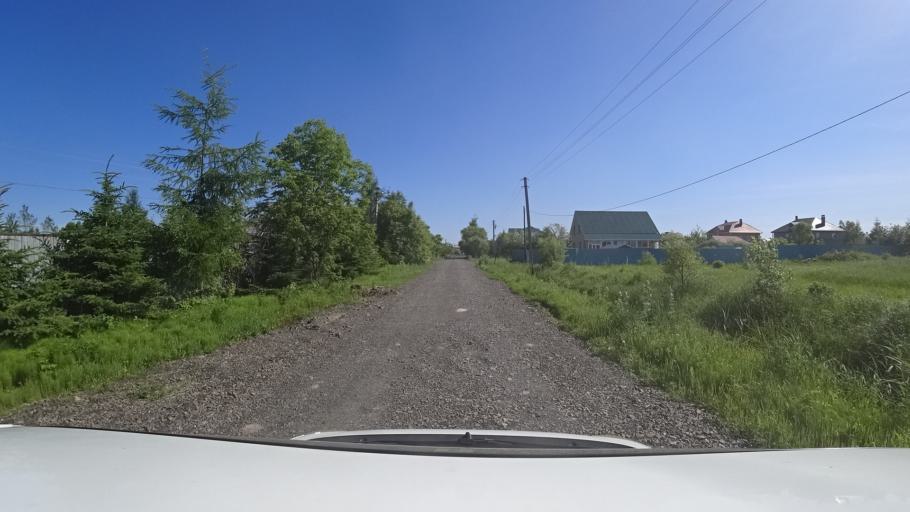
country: RU
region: Khabarovsk Krai
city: Topolevo
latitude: 48.5527
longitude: 135.1725
